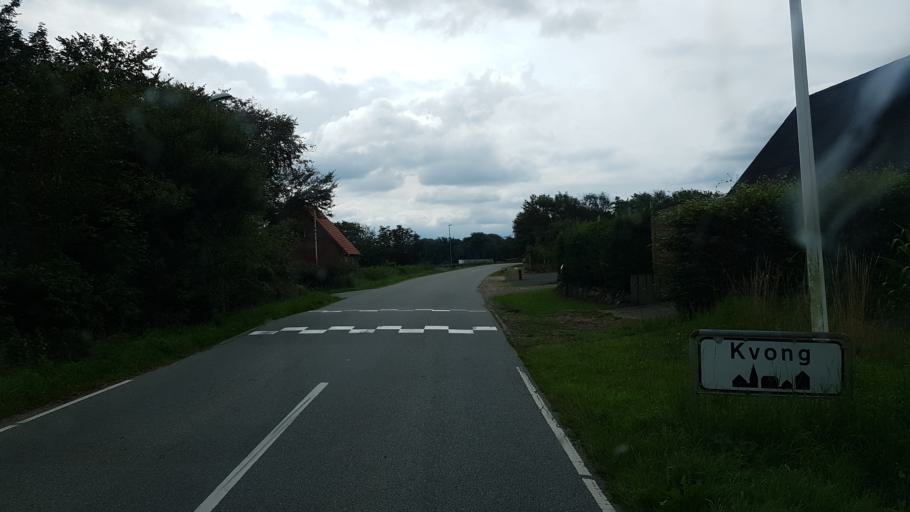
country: DK
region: South Denmark
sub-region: Varde Kommune
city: Varde
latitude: 55.7652
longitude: 8.4314
